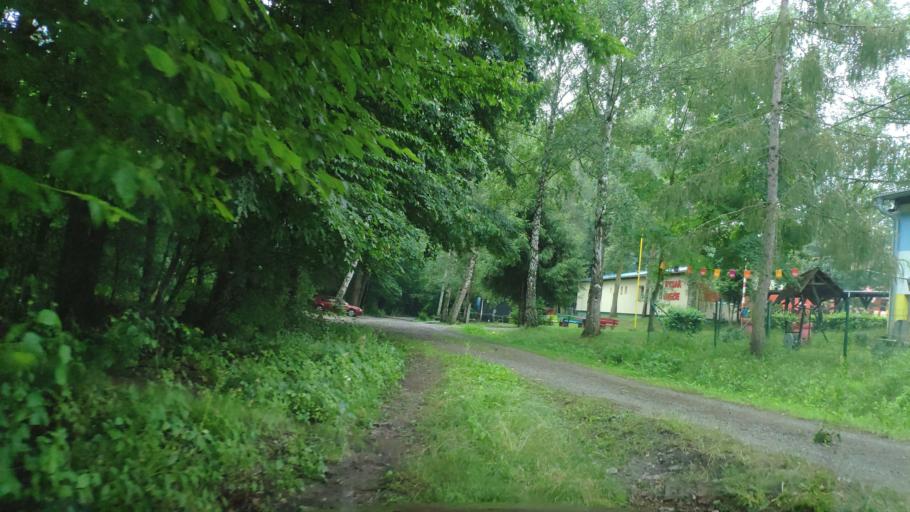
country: SK
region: Presovsky
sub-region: Okres Presov
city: Presov
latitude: 48.8626
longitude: 21.1954
